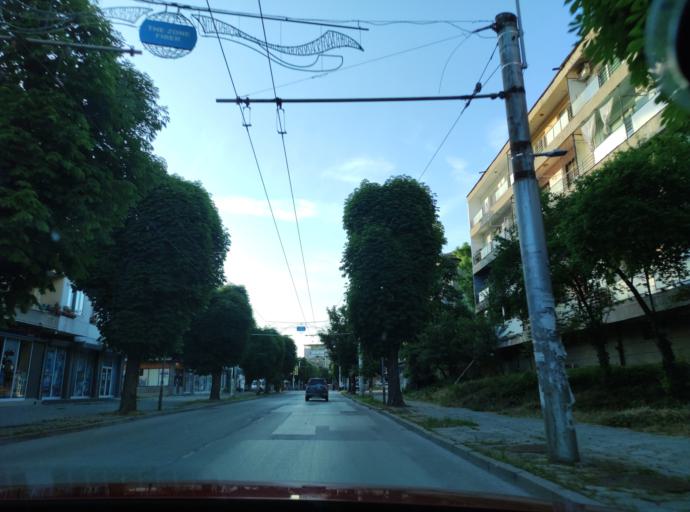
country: BG
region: Pleven
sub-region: Obshtina Pleven
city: Pleven
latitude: 43.4000
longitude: 24.6223
